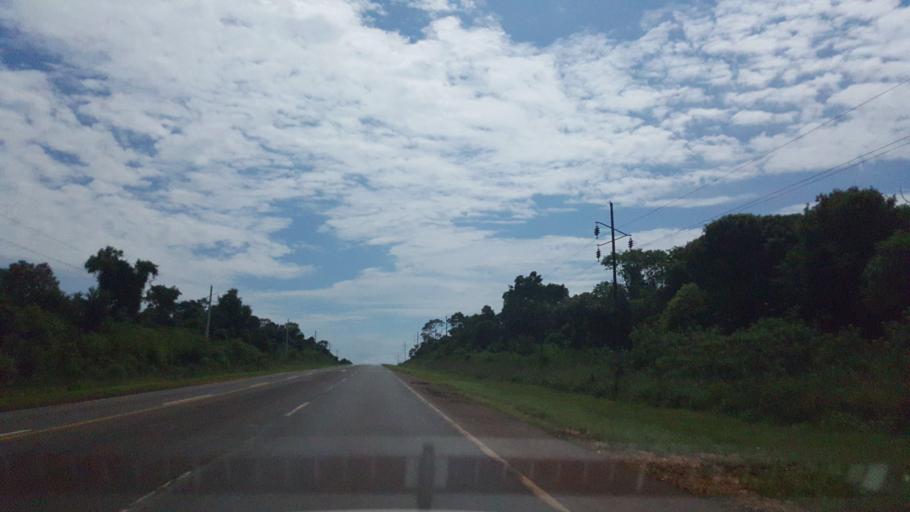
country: AR
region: Misiones
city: Capiovi
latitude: -26.8903
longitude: -55.0554
